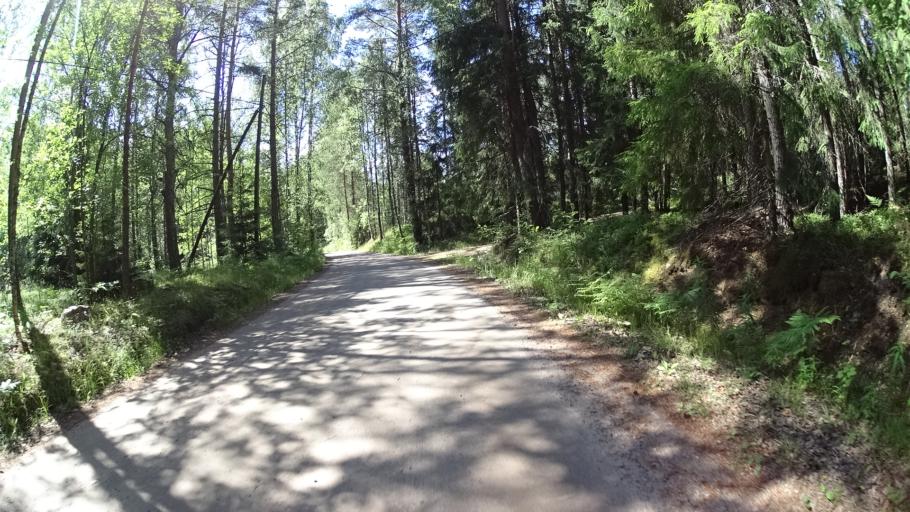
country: FI
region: Uusimaa
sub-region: Helsinki
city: Vihti
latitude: 60.3094
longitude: 24.4379
